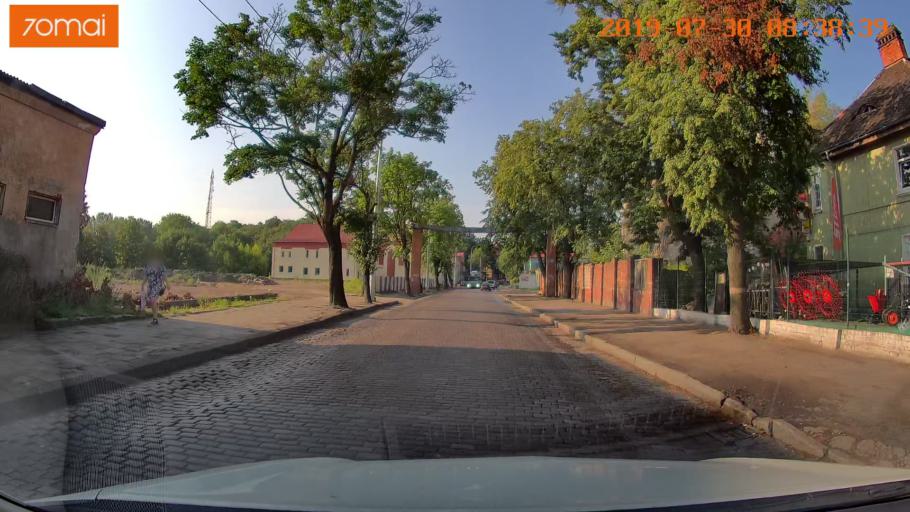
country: RU
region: Kaliningrad
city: Chernyakhovsk
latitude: 54.6340
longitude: 21.8030
